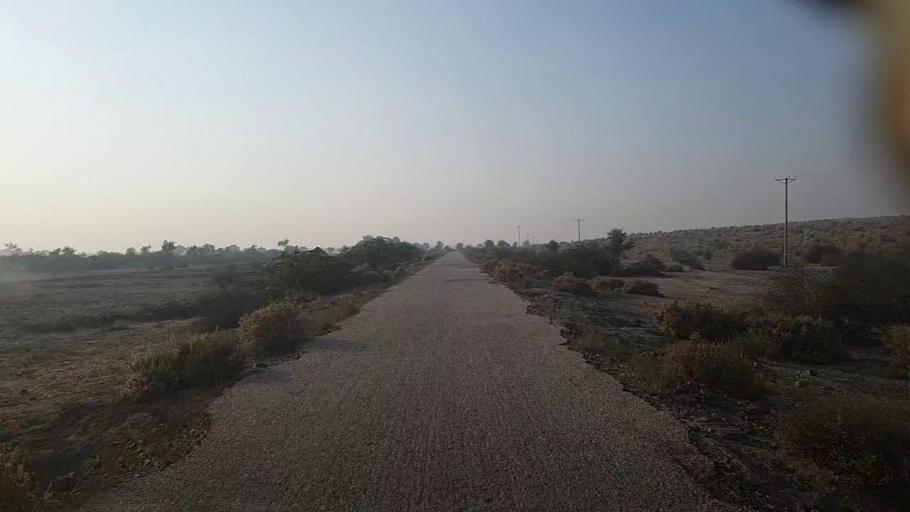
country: PK
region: Sindh
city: Pad Idan
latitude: 26.7143
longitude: 68.4686
